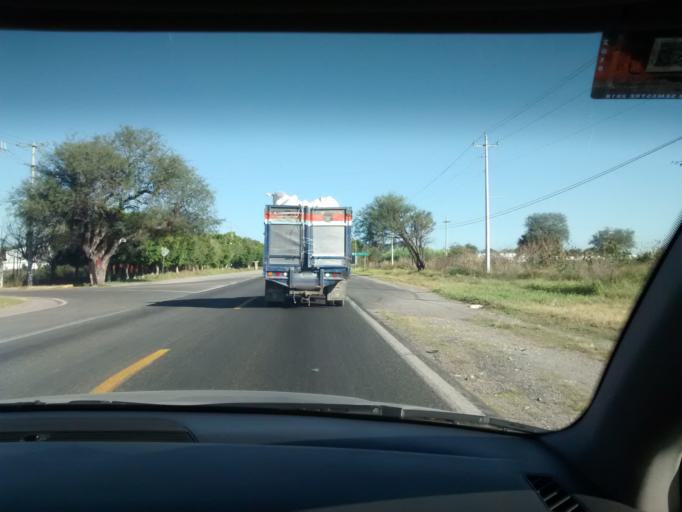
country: MX
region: Puebla
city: San Bartolo Teontepec
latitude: 18.5314
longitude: -97.5229
